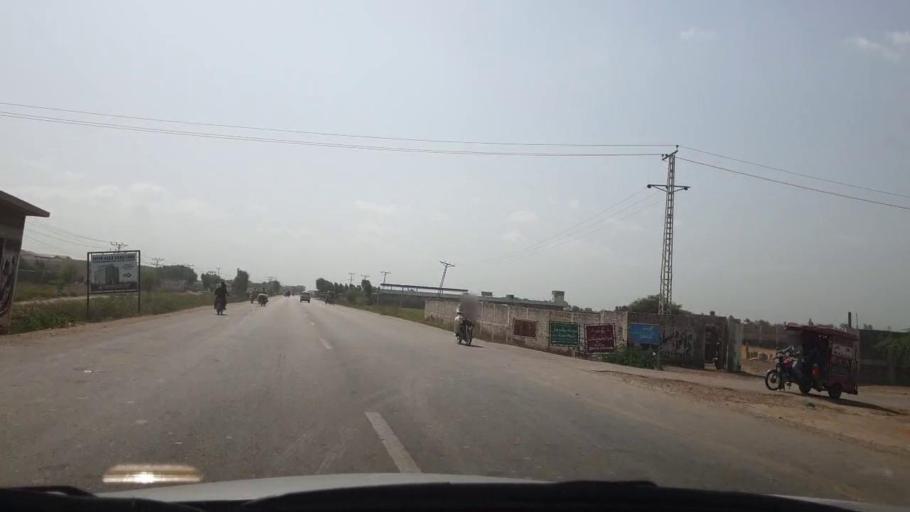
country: PK
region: Sindh
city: Matli
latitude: 24.9988
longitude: 68.6527
